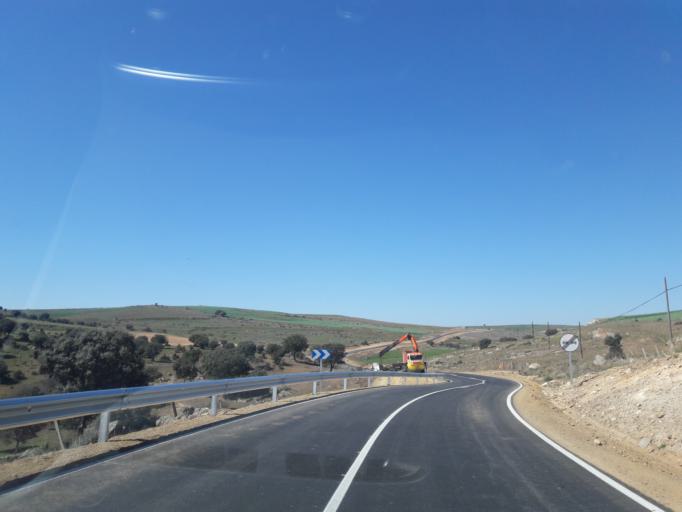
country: ES
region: Castille and Leon
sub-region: Provincia de Salamanca
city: Valdemierque
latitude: 40.8230
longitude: -5.5617
